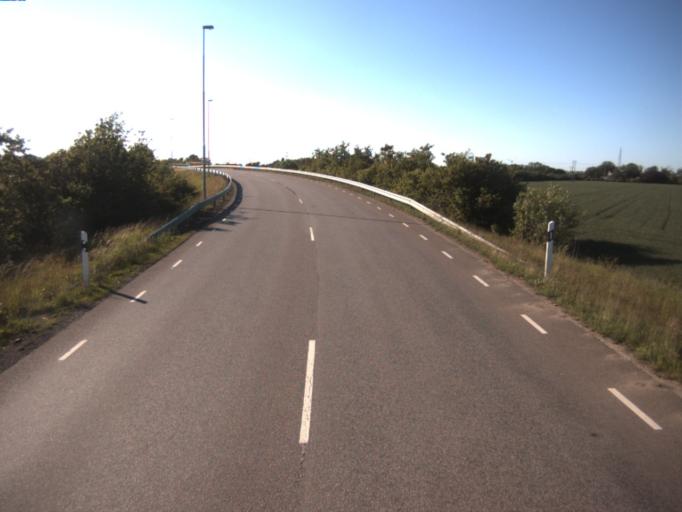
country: SE
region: Skane
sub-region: Helsingborg
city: Rydeback
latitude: 55.9697
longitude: 12.7844
